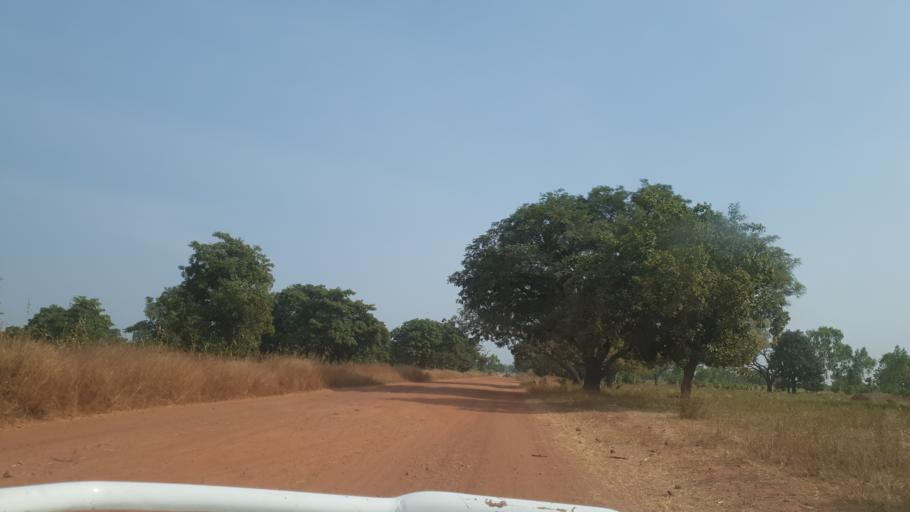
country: ML
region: Koulikoro
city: Dioila
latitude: 12.2270
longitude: -6.2163
